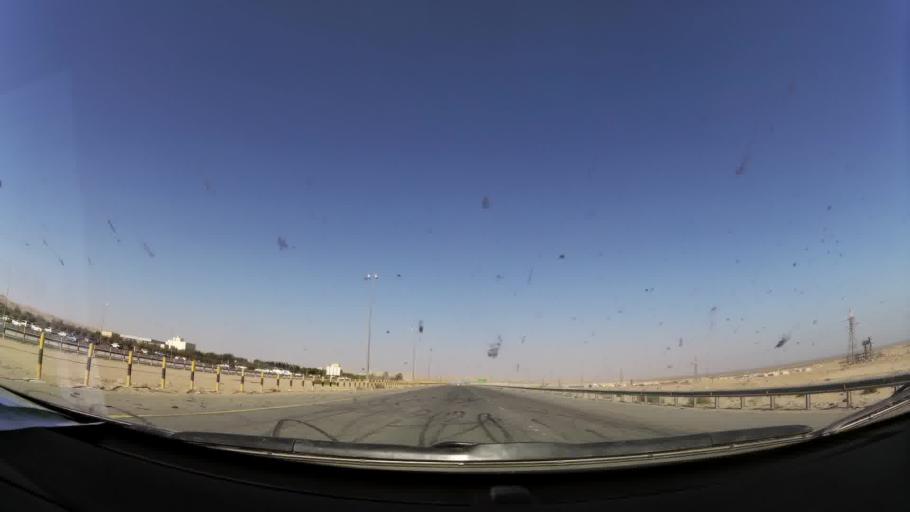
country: KW
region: Muhafazat al Jahra'
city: Al Jahra'
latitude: 29.4615
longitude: 47.7623
